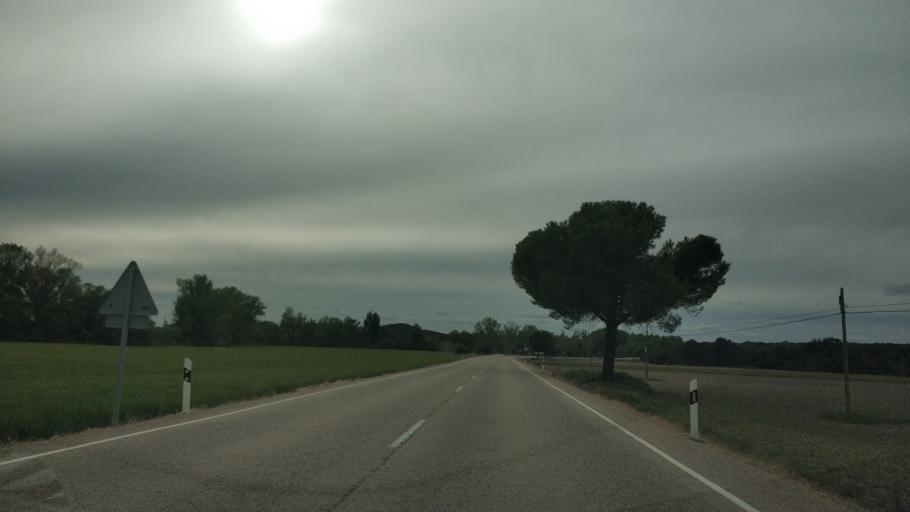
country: ES
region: Castille and Leon
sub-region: Provincia de Soria
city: Bayubas de Abajo
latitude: 41.4998
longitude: -2.8832
